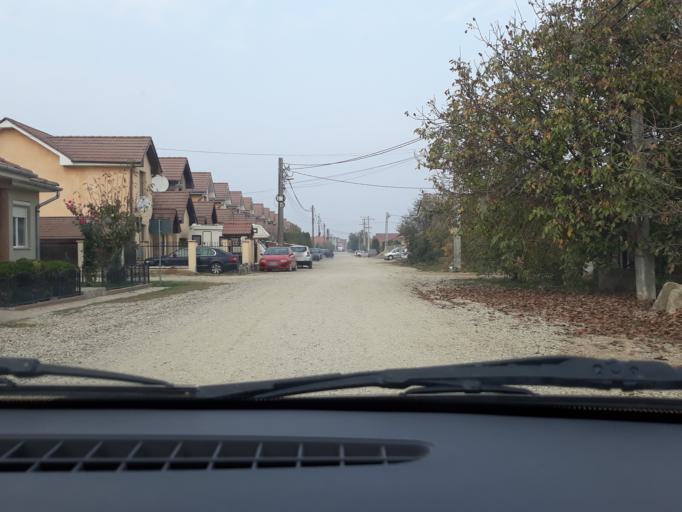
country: RO
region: Bihor
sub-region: Comuna Santandrei
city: Santandrei
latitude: 47.0617
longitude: 21.8505
